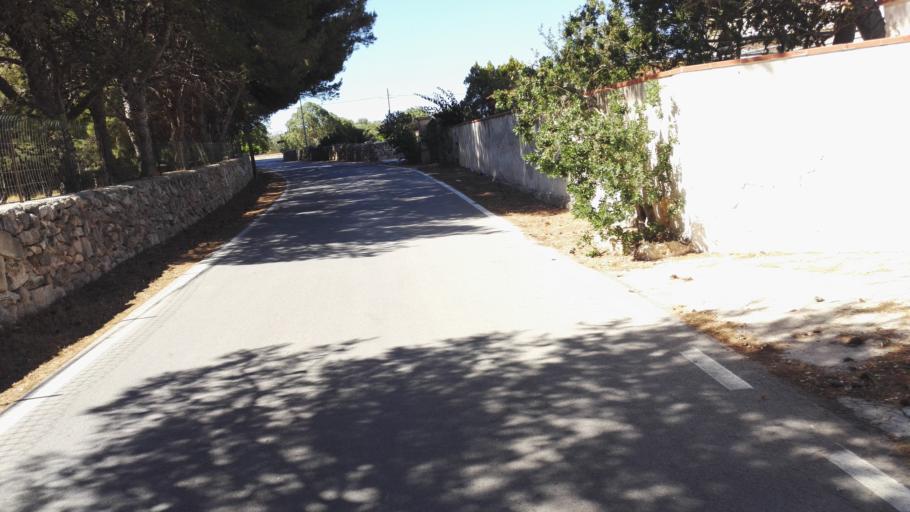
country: IT
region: Sicily
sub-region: Trapani
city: Favignana
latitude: 37.9225
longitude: 12.3375
